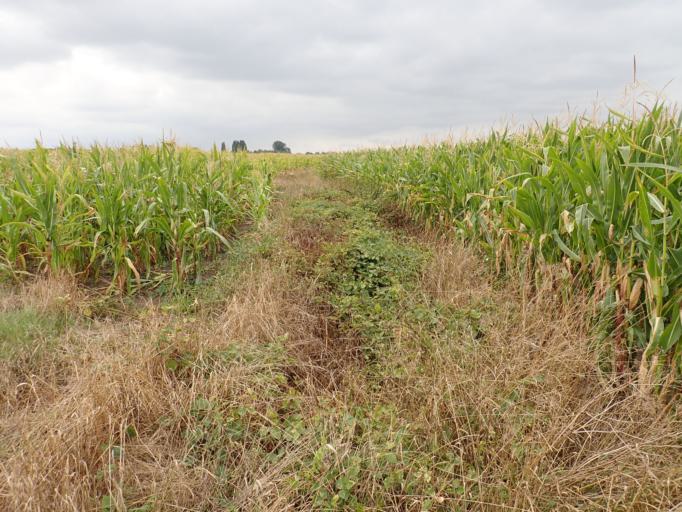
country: BE
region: Flanders
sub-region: Provincie Vlaams-Brabant
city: Kapelle-op-den-Bos
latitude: 51.0070
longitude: 4.3369
